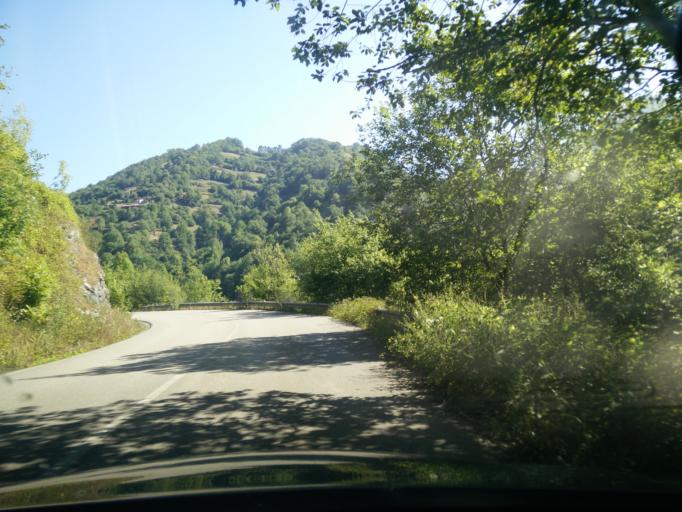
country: ES
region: Asturias
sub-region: Province of Asturias
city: Campo de Caso
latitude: 43.1892
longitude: -5.3835
